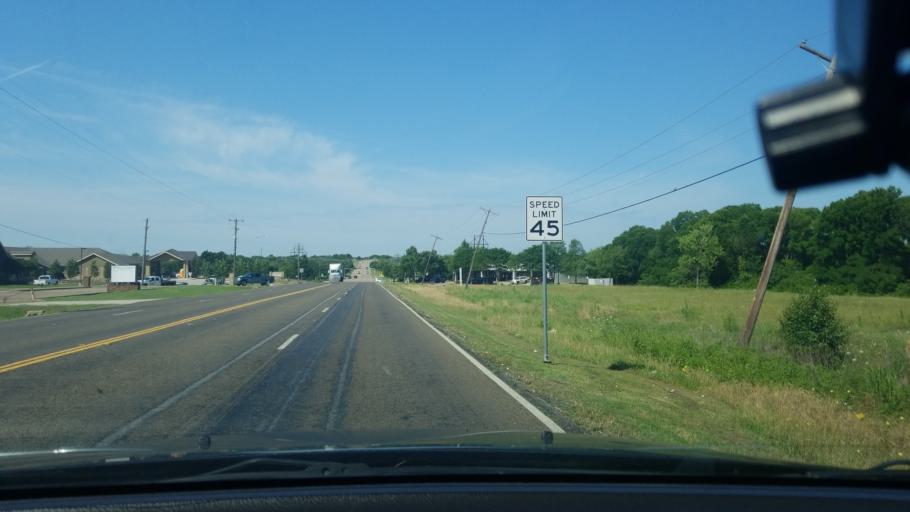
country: US
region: Texas
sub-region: Dallas County
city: Sunnyvale
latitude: 32.7741
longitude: -96.5713
